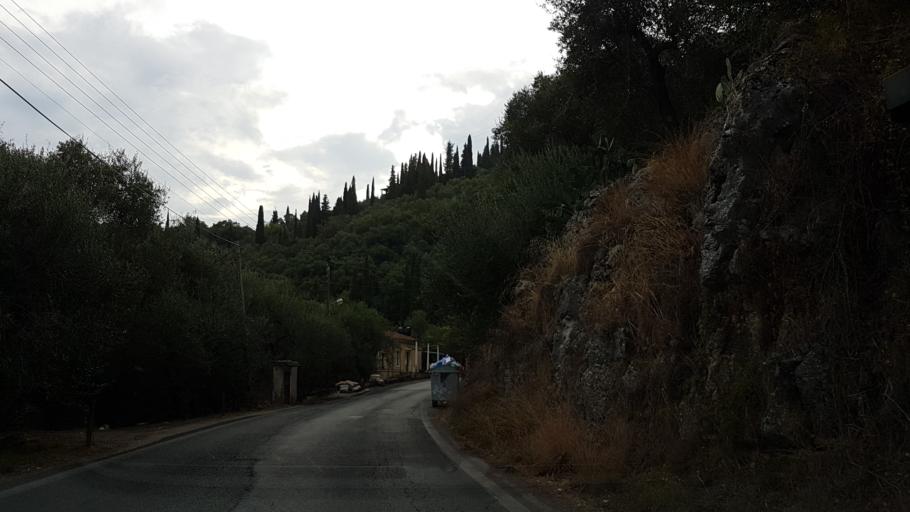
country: GR
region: Ionian Islands
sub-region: Nomos Kerkyras
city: Kerkyra
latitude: 39.7389
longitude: 19.9242
